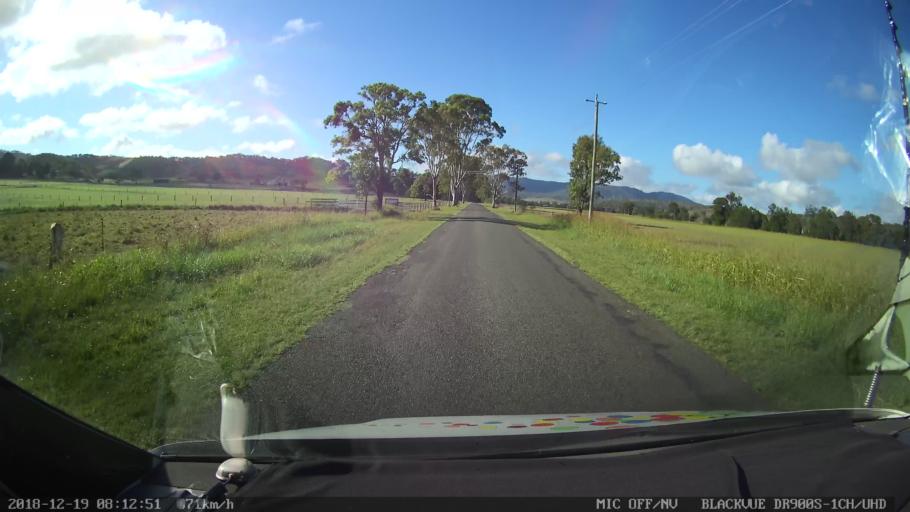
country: AU
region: Queensland
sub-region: Logan
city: Cedar Vale
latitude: -28.2319
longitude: 152.8917
